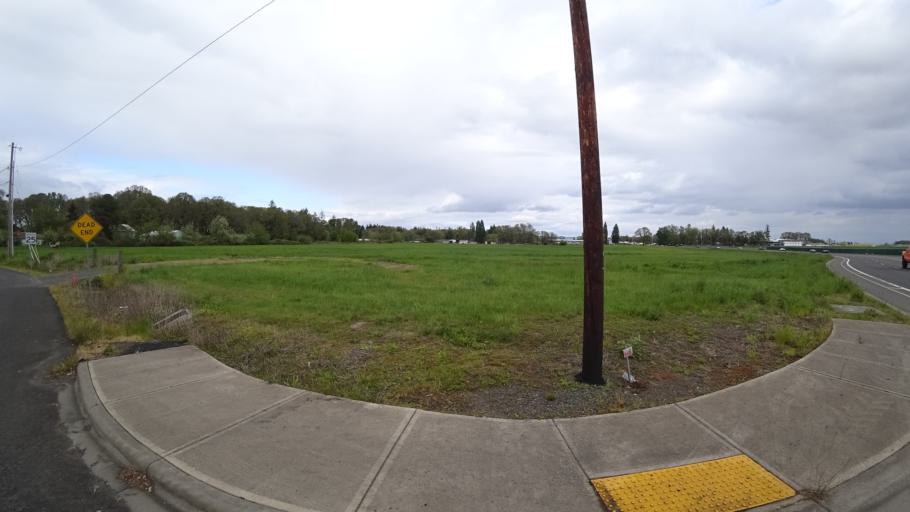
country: US
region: Oregon
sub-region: Washington County
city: Hillsboro
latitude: 45.5525
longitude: -122.9585
